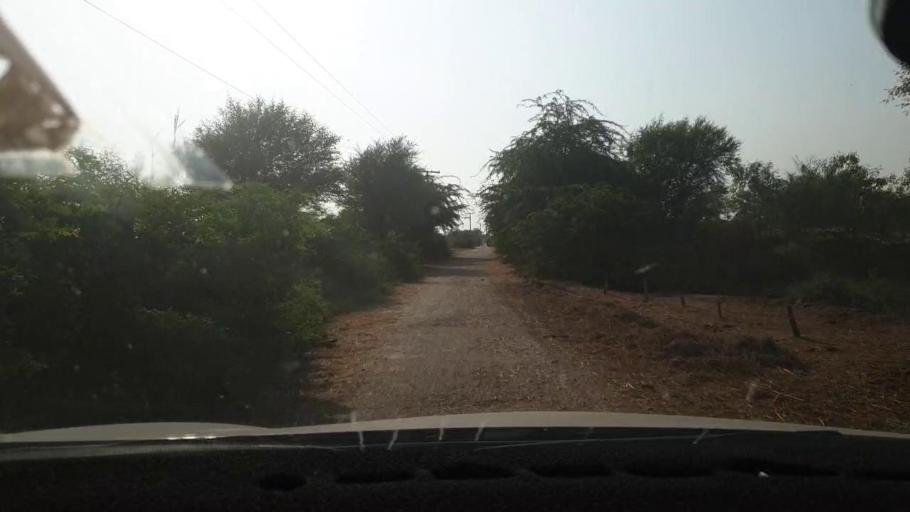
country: PK
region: Sindh
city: Berani
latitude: 25.7502
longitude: 68.7975
